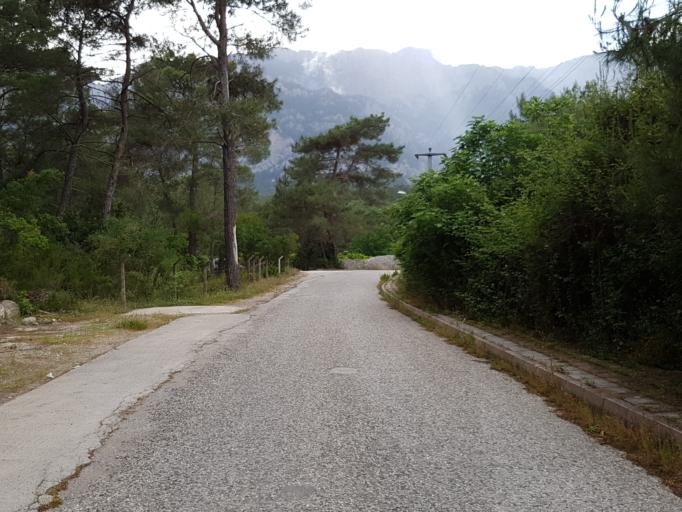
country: TR
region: Antalya
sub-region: Kemer
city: Goeynuek
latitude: 36.6428
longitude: 30.5532
